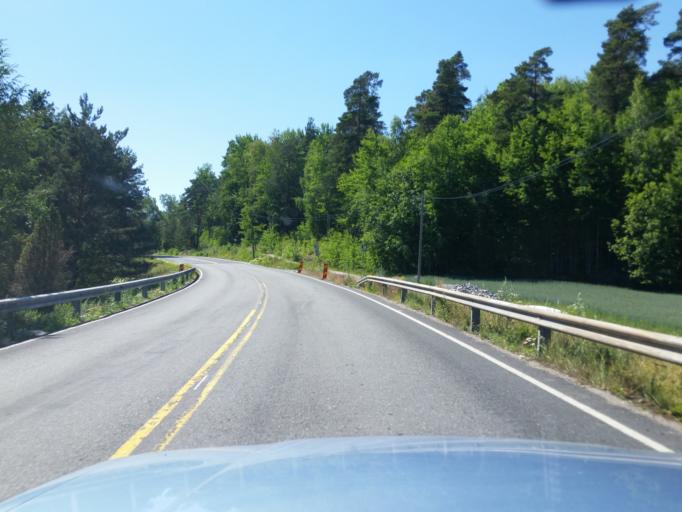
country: FI
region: Varsinais-Suomi
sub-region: Aboland-Turunmaa
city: Laensi-Turunmaa
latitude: 60.2435
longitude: 22.1764
